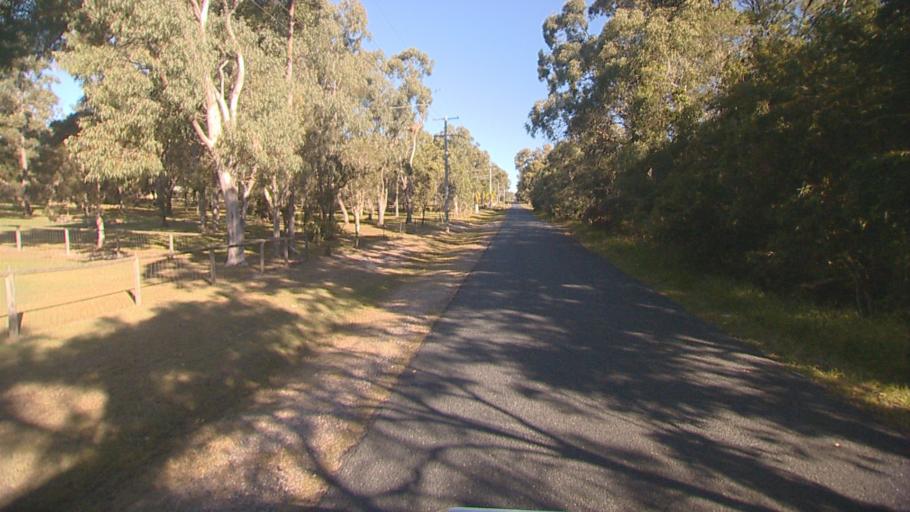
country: AU
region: Queensland
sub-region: Logan
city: Logan Reserve
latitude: -27.7137
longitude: 153.1075
